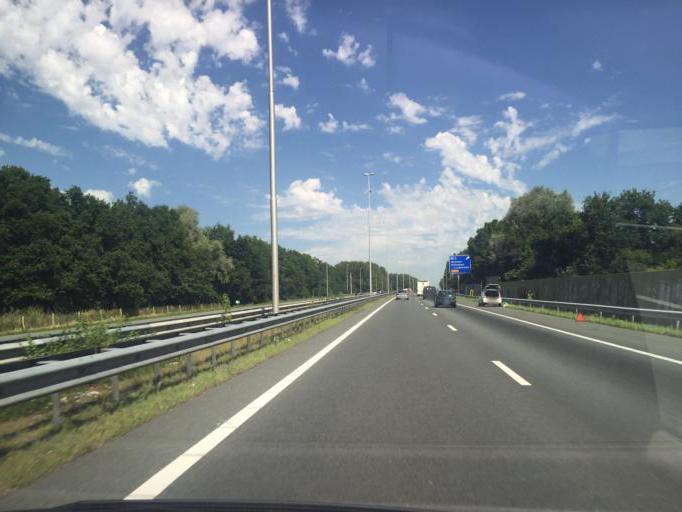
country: NL
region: Gelderland
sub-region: Gemeente Nijmegen
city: Lindenholt
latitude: 51.8165
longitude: 5.7778
